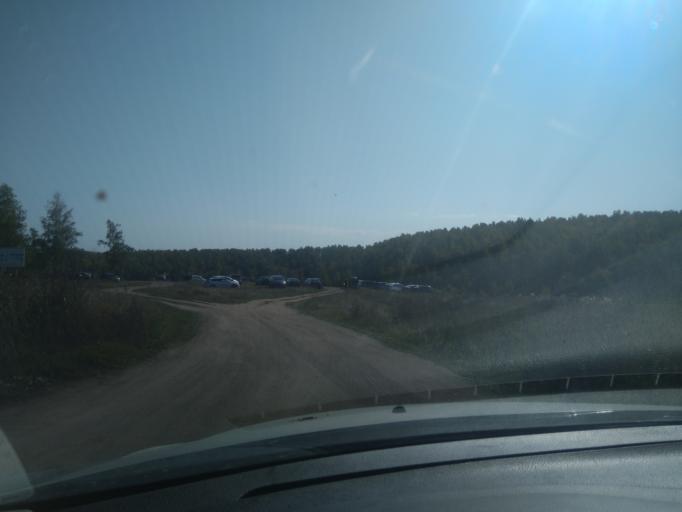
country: RU
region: Sverdlovsk
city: Pokrovskoye
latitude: 56.4350
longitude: 61.6025
